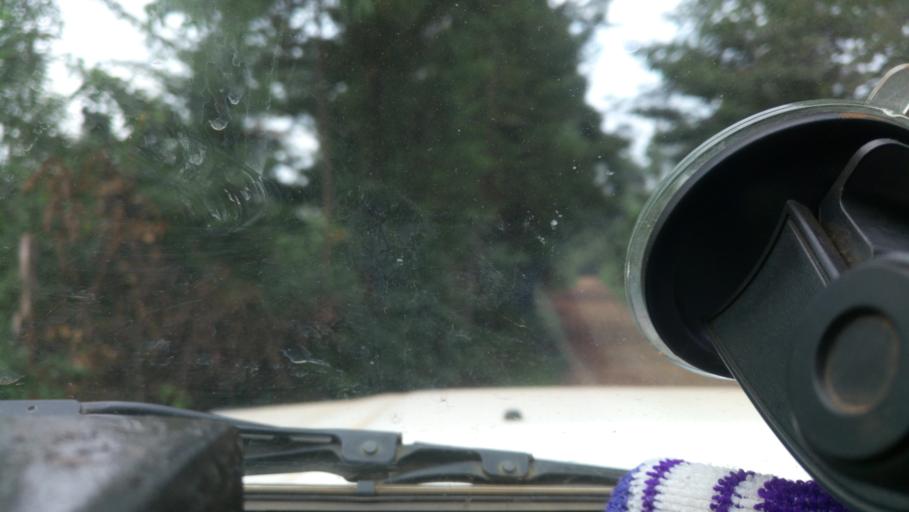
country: KE
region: Kericho
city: Sotik
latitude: -0.6493
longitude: 35.1514
